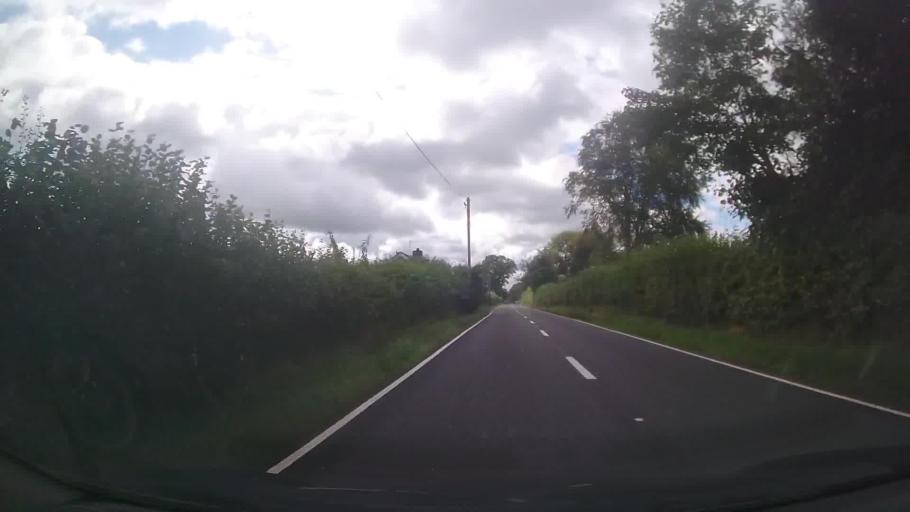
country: GB
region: Wales
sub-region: Carmarthenshire
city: Llandovery
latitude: 51.9795
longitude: -3.8357
